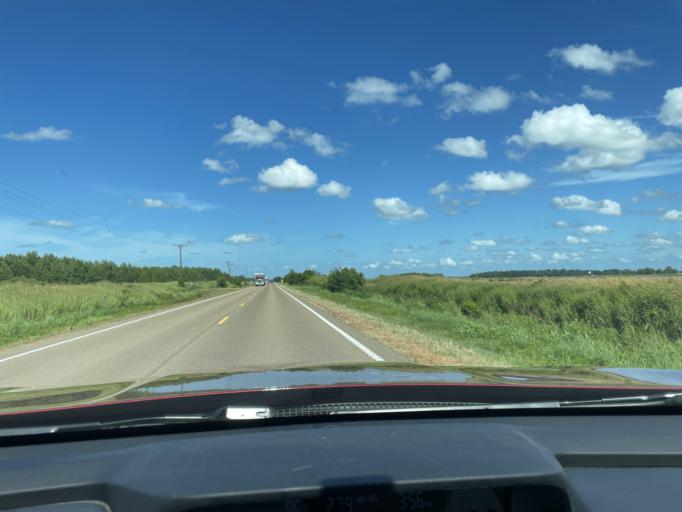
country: US
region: Mississippi
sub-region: Humphreys County
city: Belzoni
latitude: 33.1829
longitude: -90.6174
